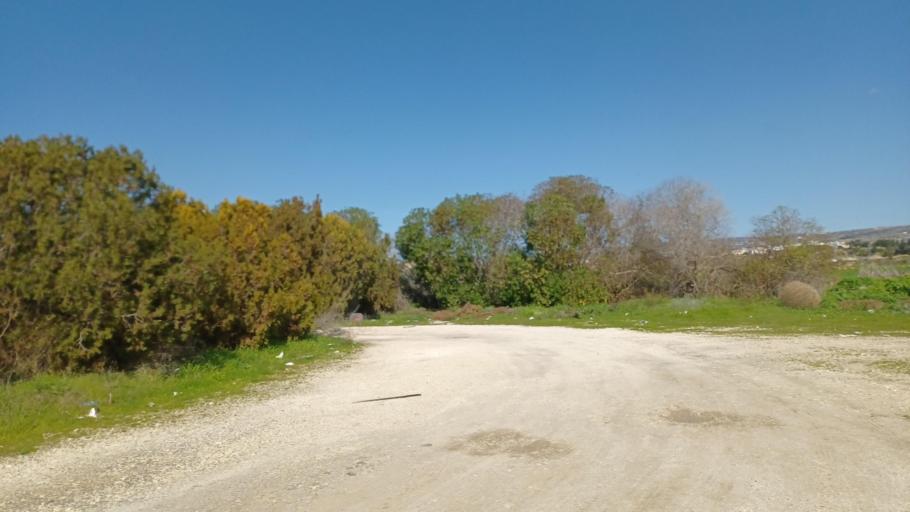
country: CY
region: Pafos
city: Paphos
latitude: 34.7478
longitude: 32.4389
